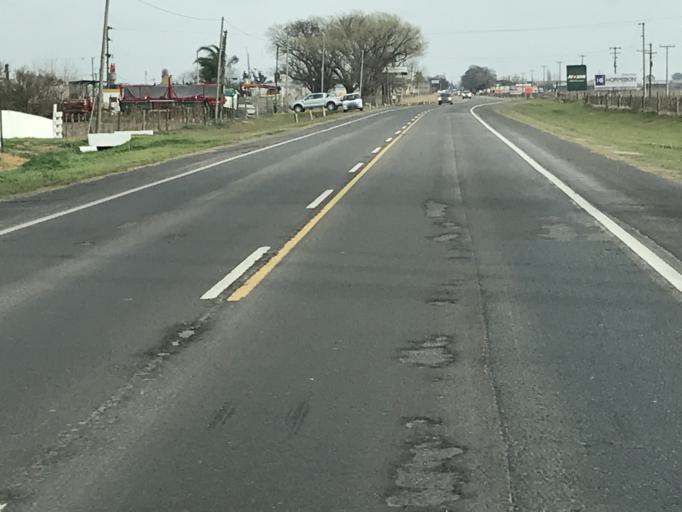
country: AR
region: Santa Fe
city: Armstrong
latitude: -32.7778
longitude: -61.5835
